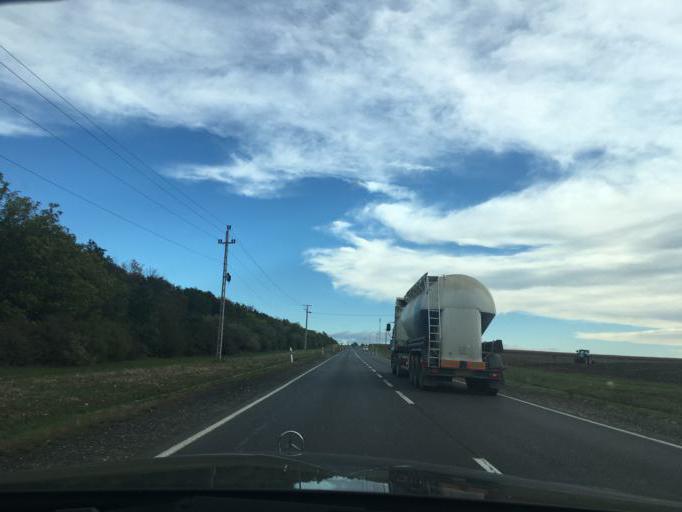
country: HU
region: Borsod-Abauj-Zemplen
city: Arnot
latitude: 48.1454
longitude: 20.8899
